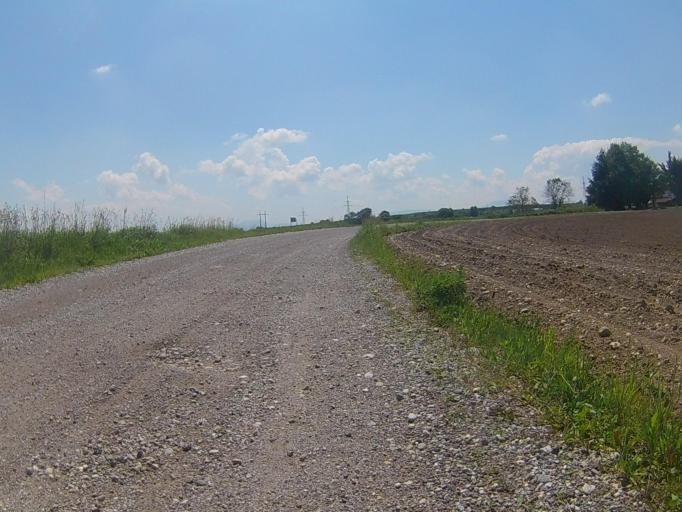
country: SI
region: Hoce-Slivnica
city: Radizel
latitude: 46.4840
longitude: 15.6652
